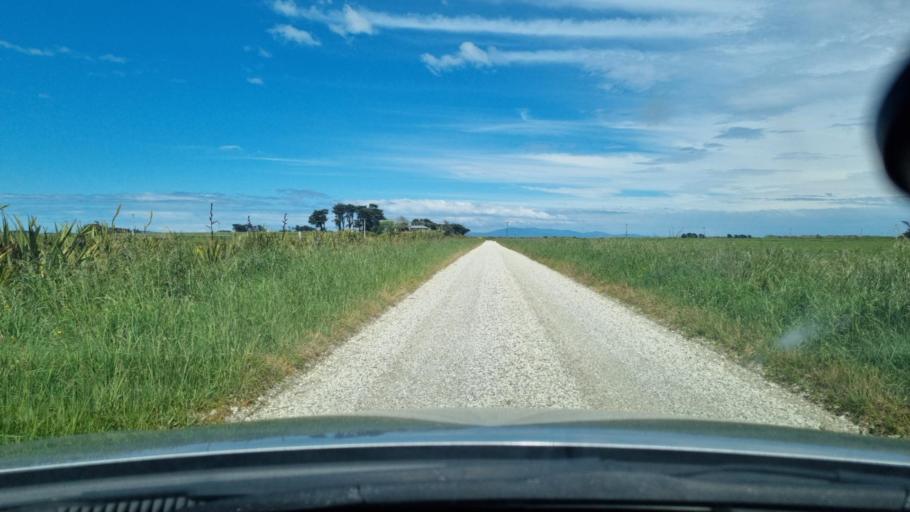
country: NZ
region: Southland
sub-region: Invercargill City
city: Invercargill
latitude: -46.3879
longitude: 168.2619
